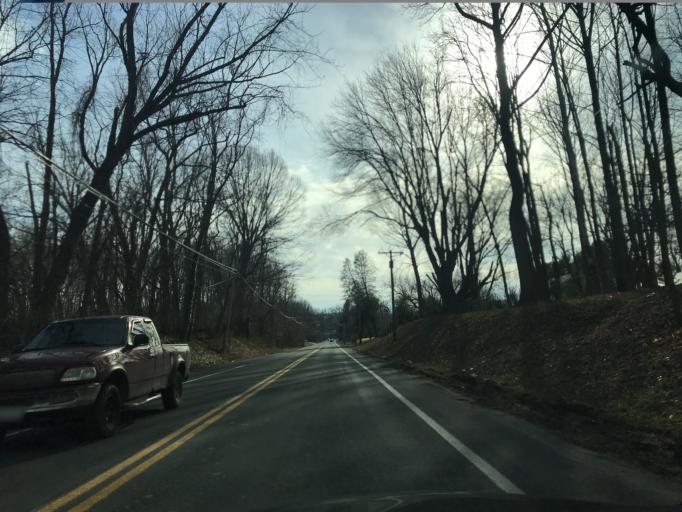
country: US
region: Maryland
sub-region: Prince George's County
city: Woodmore
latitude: 38.9347
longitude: -76.8038
